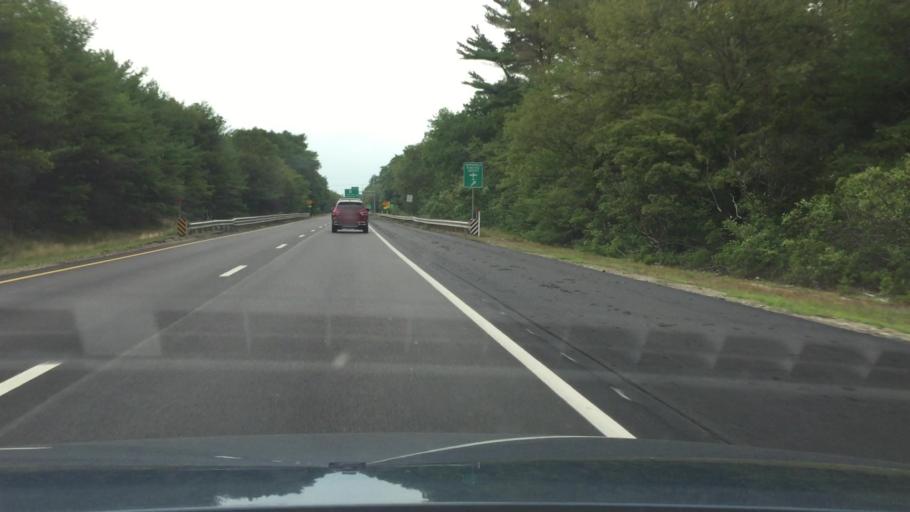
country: US
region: Massachusetts
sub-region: Plymouth County
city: Marshfield
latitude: 42.0497
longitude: -70.7234
